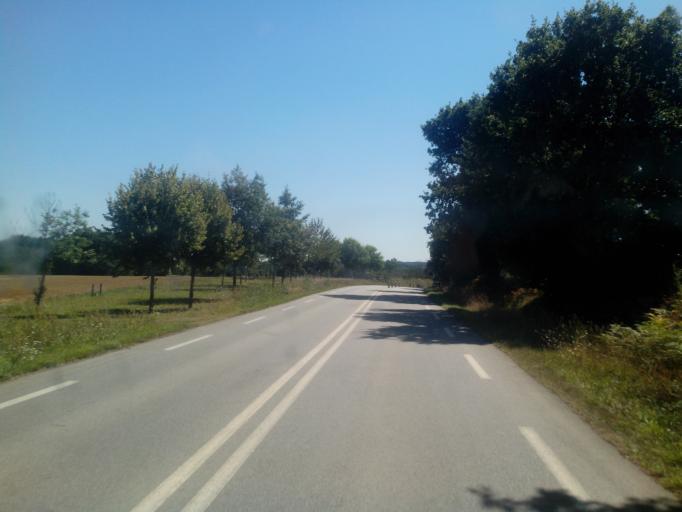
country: FR
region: Brittany
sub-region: Departement du Morbihan
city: Josselin
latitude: 47.9456
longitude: -2.5452
